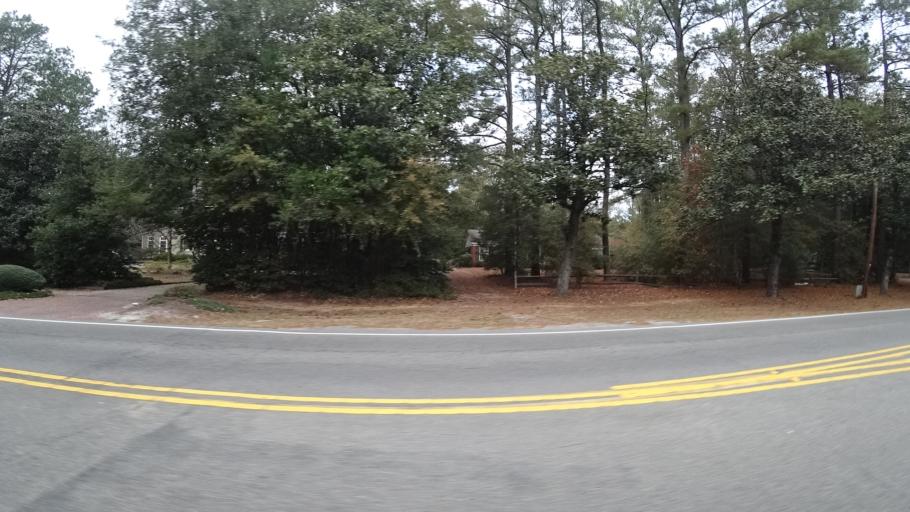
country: US
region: North Carolina
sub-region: Moore County
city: Pinehurst
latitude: 35.1970
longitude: -79.4623
